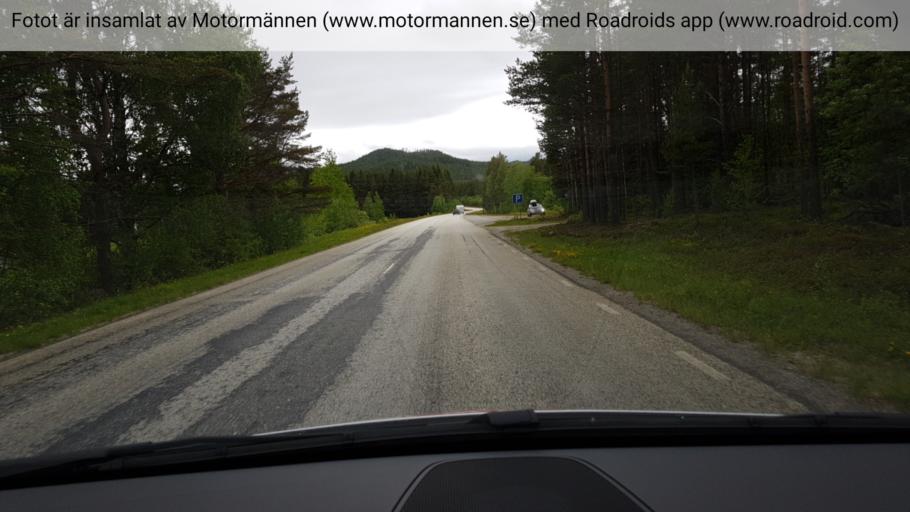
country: SE
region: Jaemtland
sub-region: Harjedalens Kommun
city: Sveg
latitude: 62.4124
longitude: 13.6394
